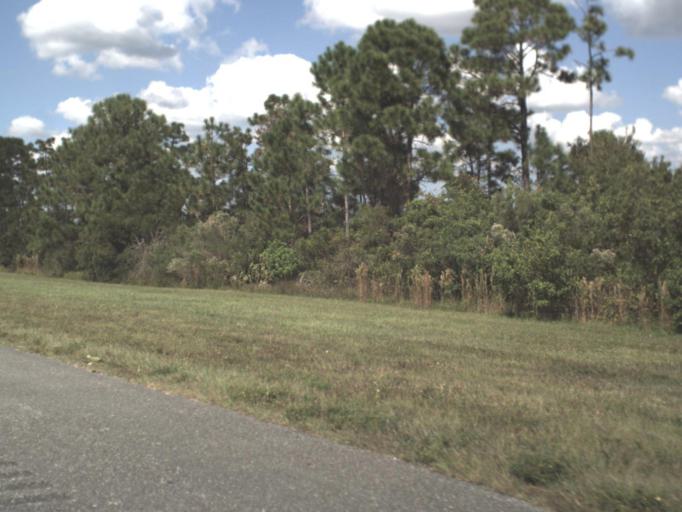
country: US
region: Florida
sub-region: Indian River County
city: Fellsmere
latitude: 27.7625
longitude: -80.9512
